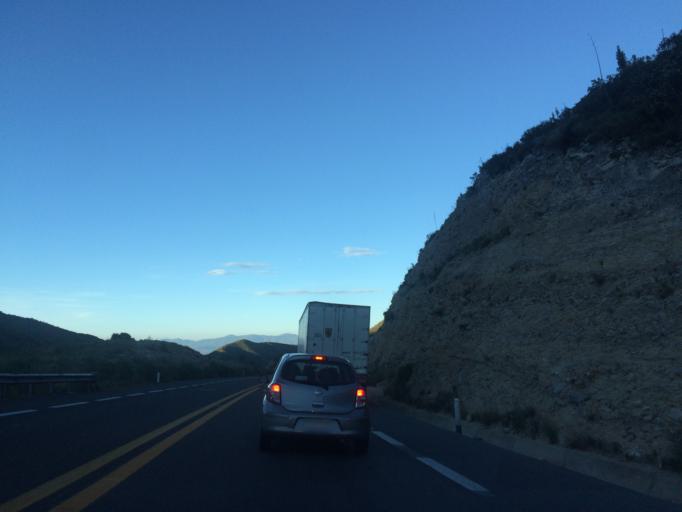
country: MX
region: Puebla
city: Chapuco
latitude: 18.6388
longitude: -97.4584
